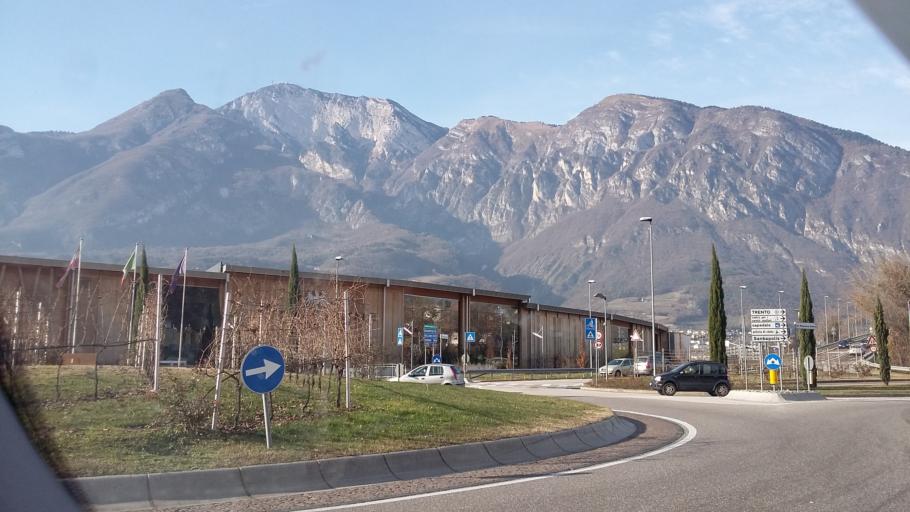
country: IT
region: Trentino-Alto Adige
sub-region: Provincia di Trento
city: Ravina
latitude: 46.0325
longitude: 11.1322
